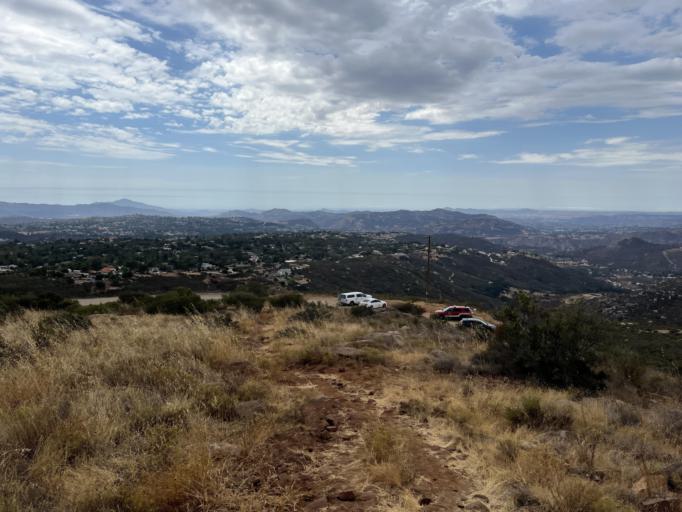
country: US
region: California
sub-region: San Diego County
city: Alpine
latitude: 32.8569
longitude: -116.7415
